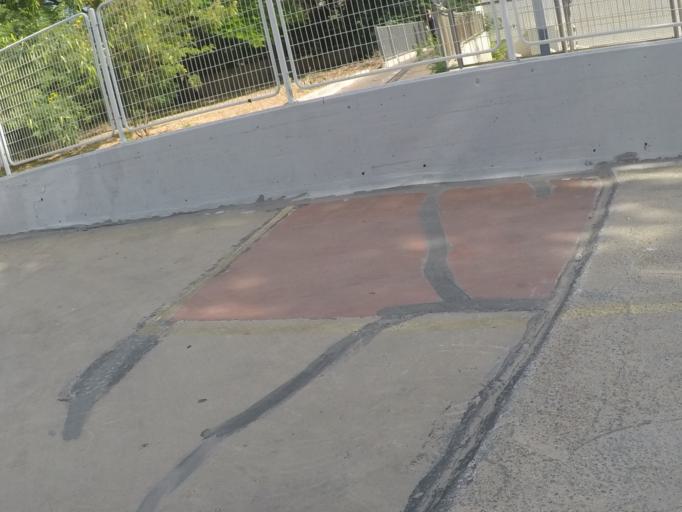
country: IL
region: Tel Aviv
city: Ramat Gan
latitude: 32.1114
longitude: 34.7943
